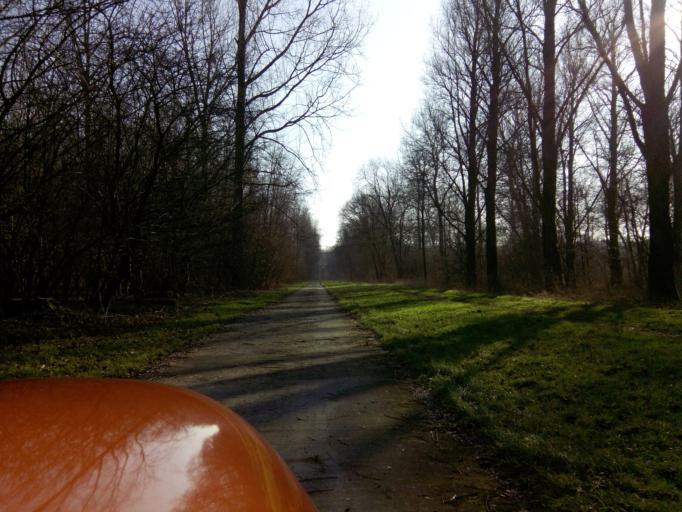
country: NL
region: Flevoland
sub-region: Gemeente Zeewolde
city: Zeewolde
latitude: 52.2966
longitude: 5.5032
